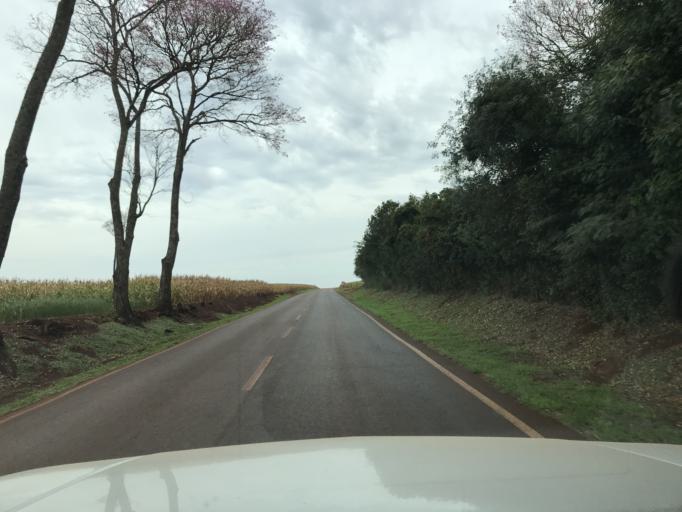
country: BR
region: Parana
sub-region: Palotina
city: Palotina
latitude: -24.4381
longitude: -53.9147
